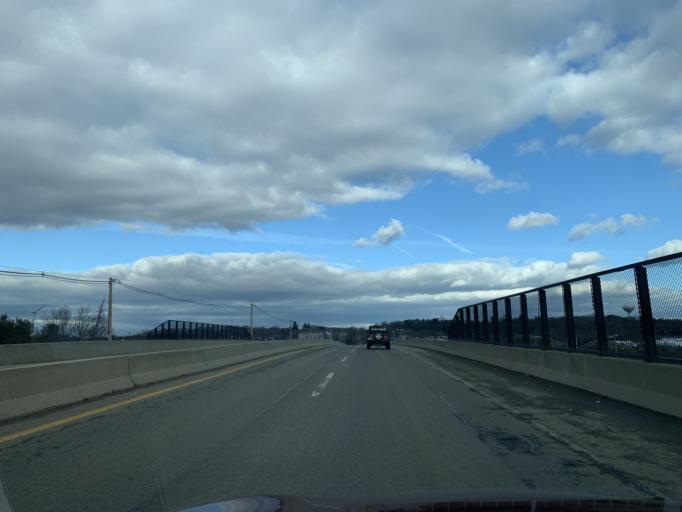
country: US
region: Massachusetts
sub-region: Essex County
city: Newburyport
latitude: 42.7941
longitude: -70.8770
